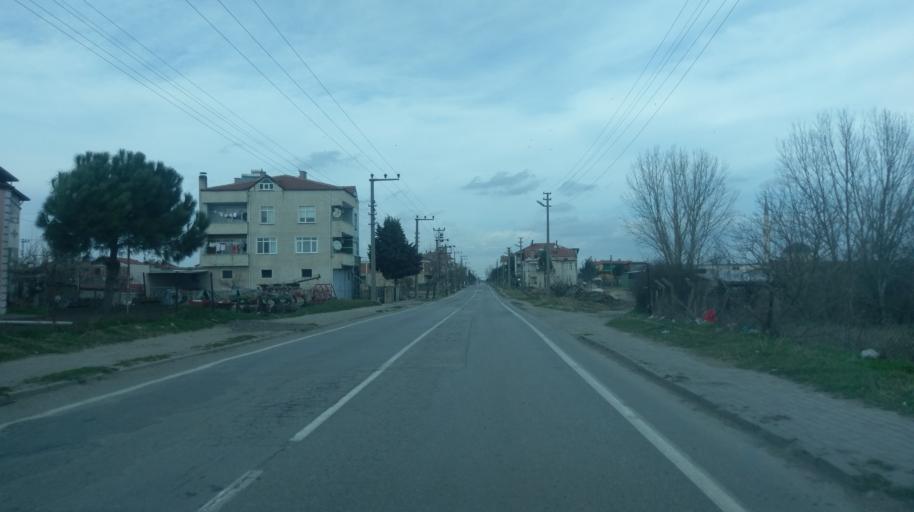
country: TR
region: Edirne
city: Havsa
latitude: 41.5569
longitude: 26.8250
